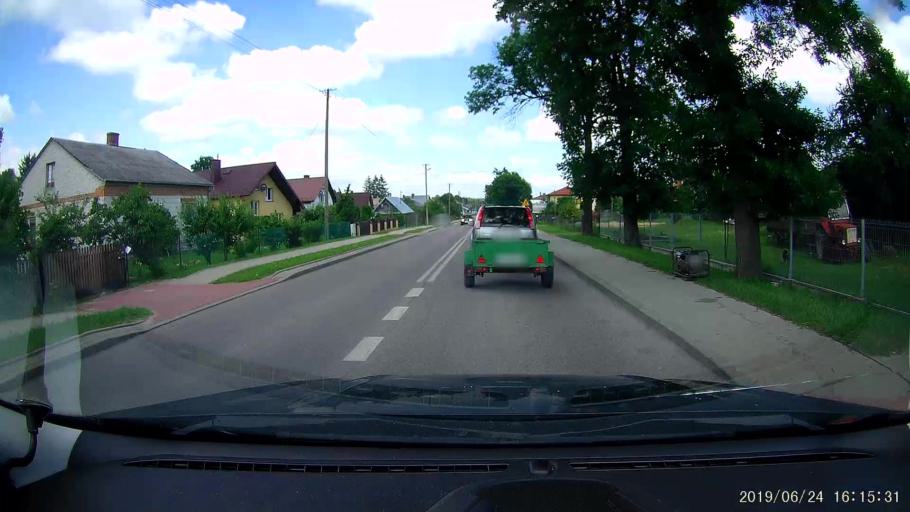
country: PL
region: Lublin Voivodeship
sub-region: Powiat tomaszowski
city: Belzec
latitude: 50.3794
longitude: 23.4011
